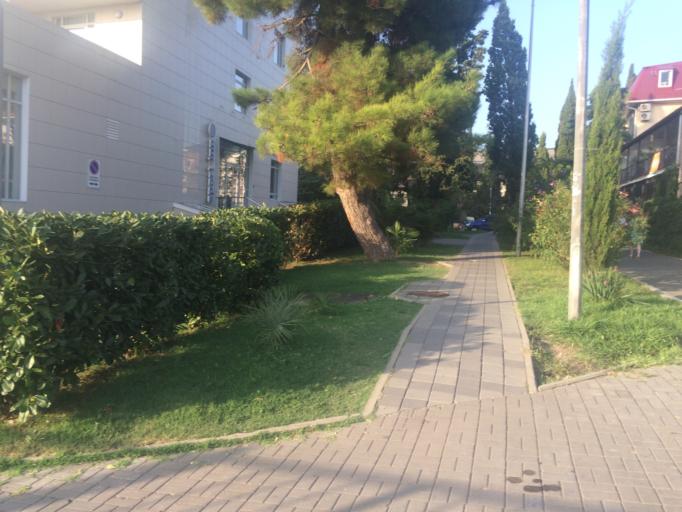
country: RU
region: Krasnodarskiy
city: Adler
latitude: 43.3890
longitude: 39.9865
